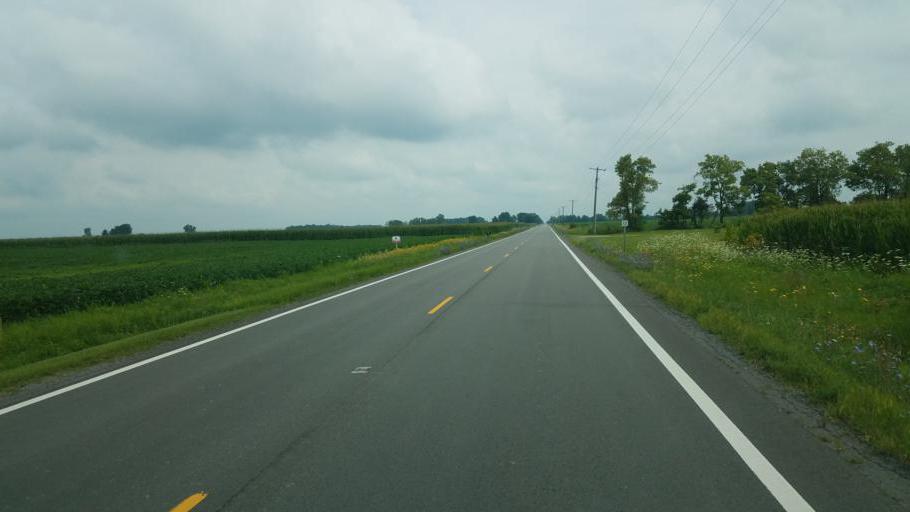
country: US
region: Ohio
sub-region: Marion County
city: Marion
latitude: 40.6438
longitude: -83.0216
